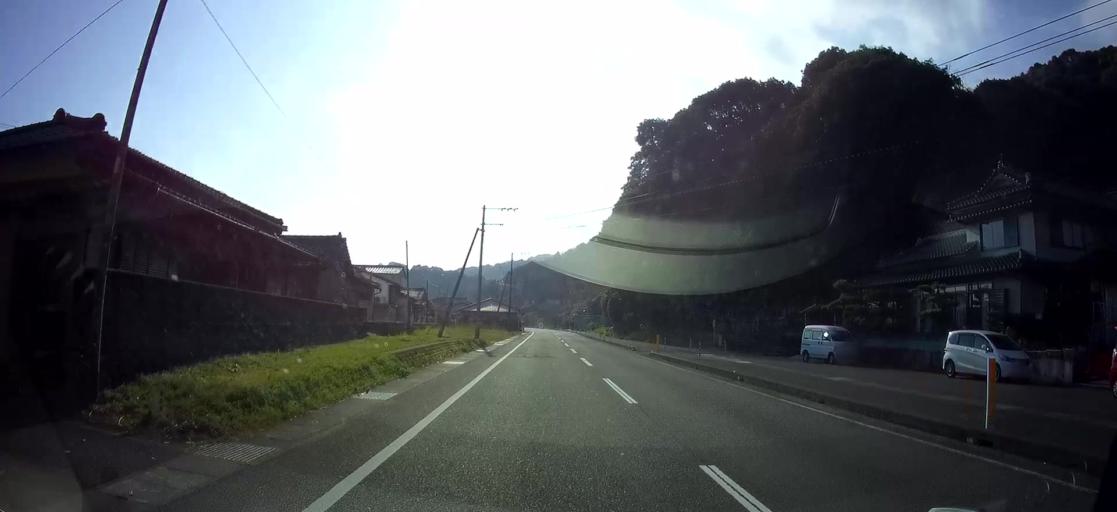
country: JP
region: Kumamoto
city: Yatsushiro
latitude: 32.4503
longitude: 130.4184
